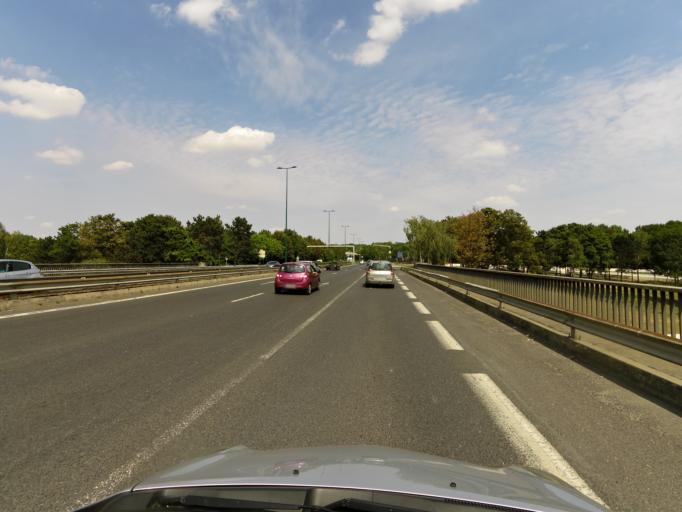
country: FR
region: Champagne-Ardenne
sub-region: Departement de la Marne
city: Reims
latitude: 49.2339
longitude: 4.0400
